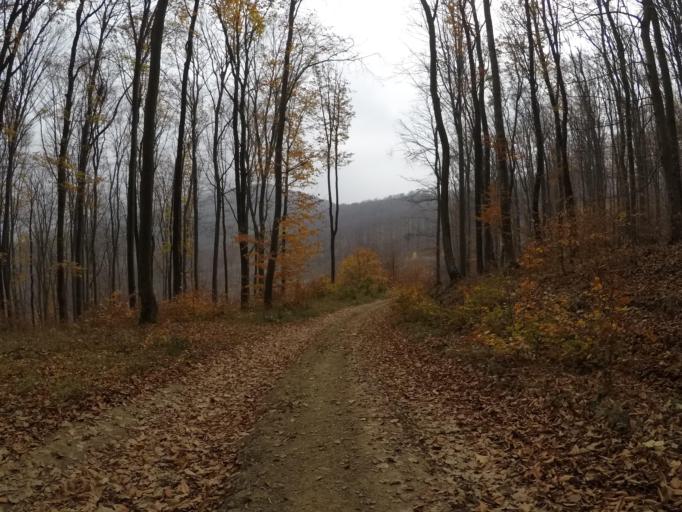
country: SK
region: Presovsky
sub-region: Okres Presov
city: Presov
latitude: 48.8863
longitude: 21.1746
